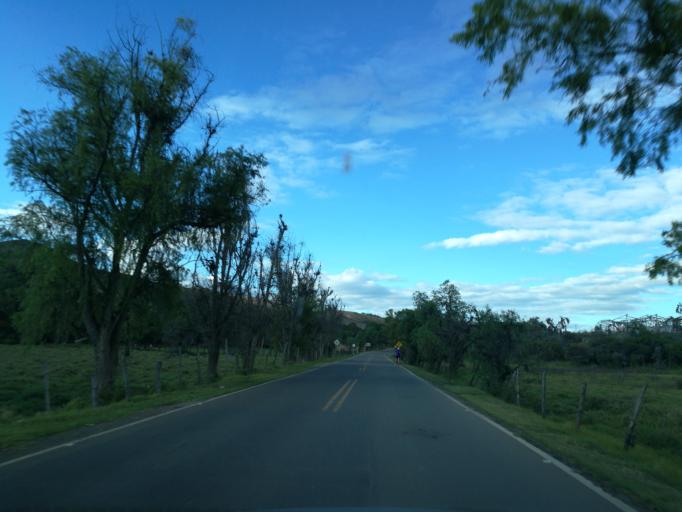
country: CO
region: Boyaca
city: Sutamarchan
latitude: 5.6149
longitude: -73.6240
